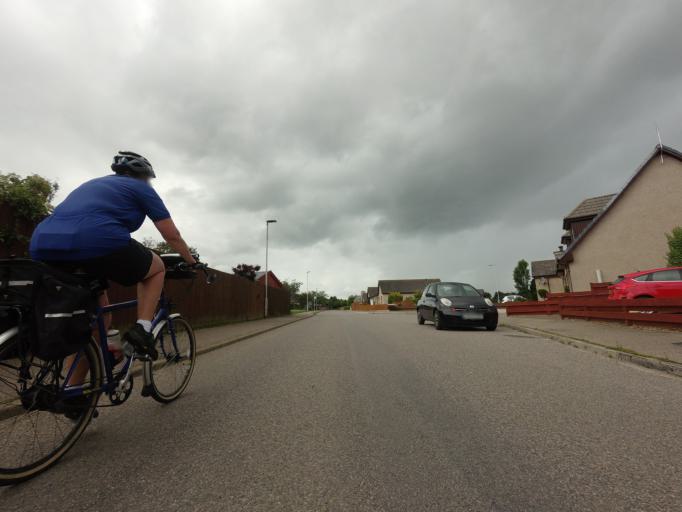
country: GB
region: Scotland
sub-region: Moray
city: Fochabers
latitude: 57.6629
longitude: -3.1145
